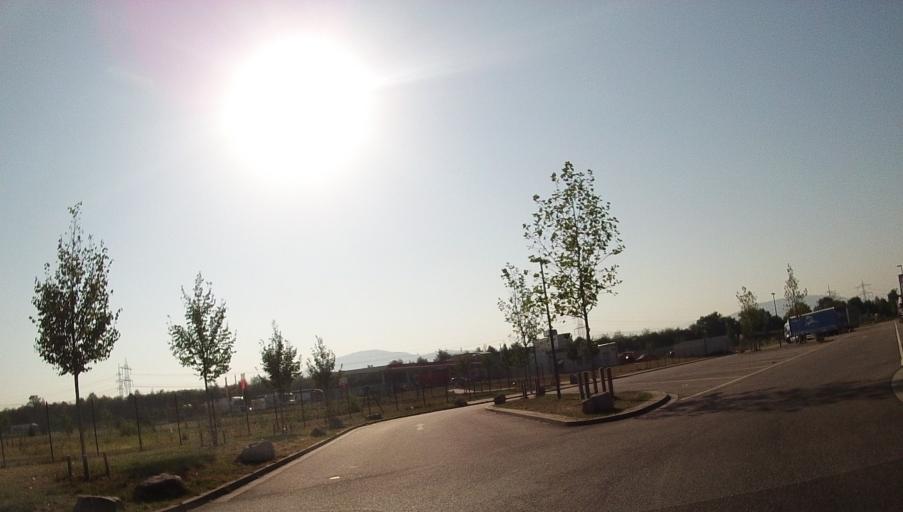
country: DE
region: Baden-Wuerttemberg
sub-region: Karlsruhe Region
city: Iffezheim
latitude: 48.8113
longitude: 8.1831
